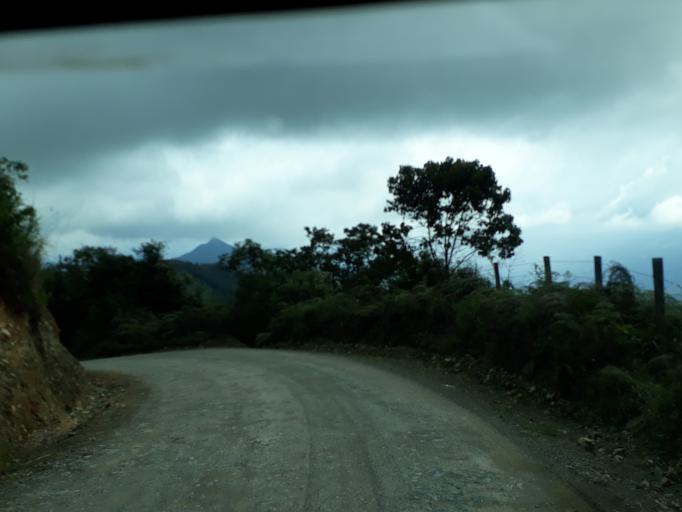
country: CO
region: Cundinamarca
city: Pacho
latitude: 5.2357
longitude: -74.1856
